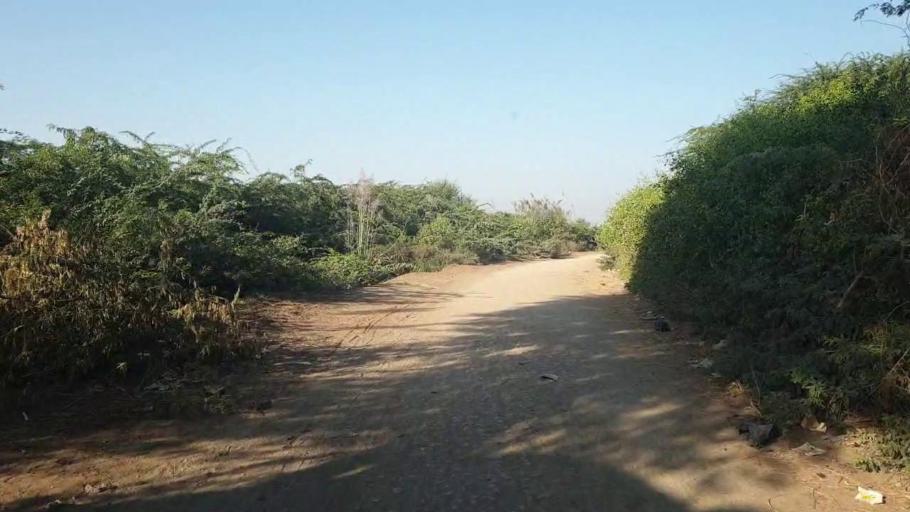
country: PK
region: Sindh
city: Badin
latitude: 24.6868
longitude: 68.8168
